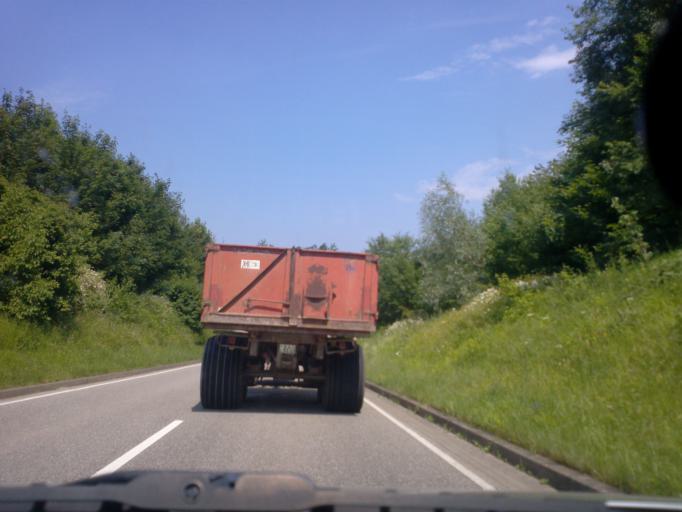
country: DE
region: Baden-Wuerttemberg
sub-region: Karlsruhe Region
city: Bretten
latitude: 49.0041
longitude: 8.6677
